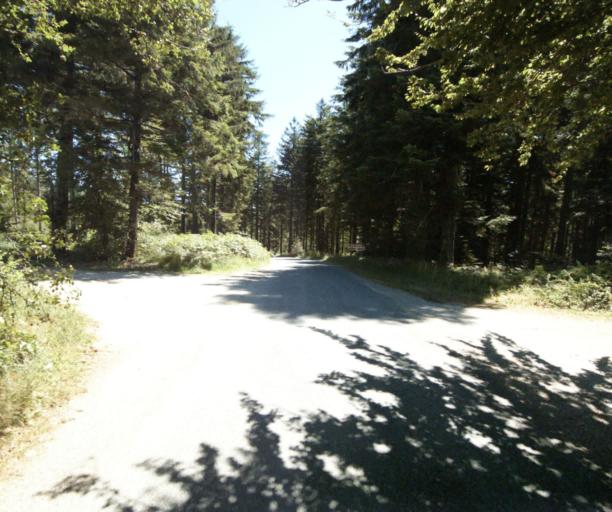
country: FR
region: Midi-Pyrenees
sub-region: Departement du Tarn
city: Dourgne
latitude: 43.4246
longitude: 2.1810
